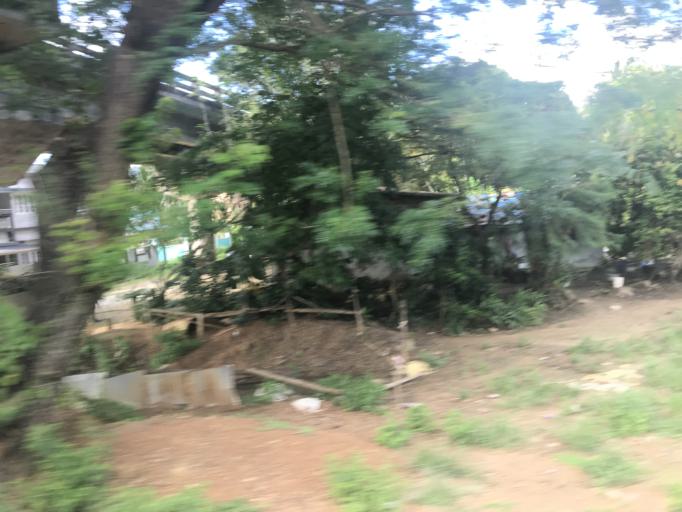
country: IN
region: Kerala
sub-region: Palakkad district
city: Palakkad
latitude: 10.8133
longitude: 76.6637
